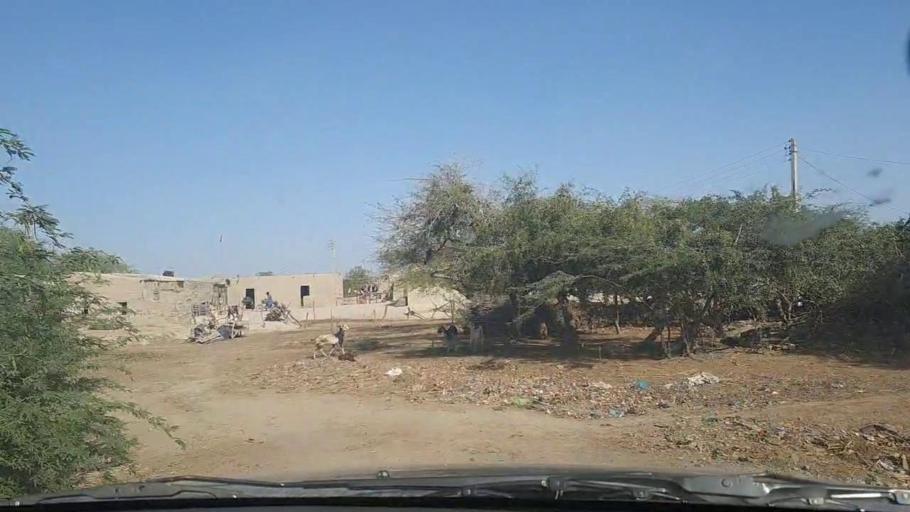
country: PK
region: Sindh
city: Chuhar Jamali
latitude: 24.3233
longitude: 67.7679
